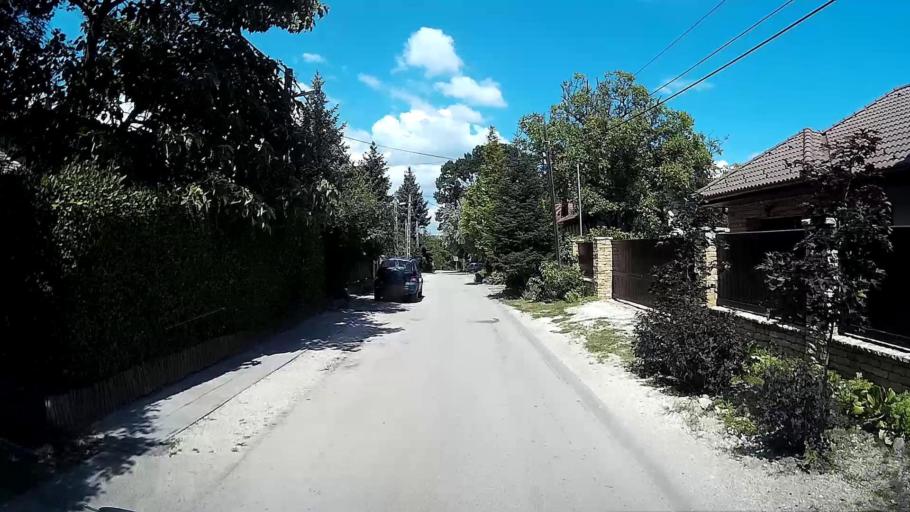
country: HU
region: Pest
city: Szentendre
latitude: 47.6691
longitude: 19.0629
